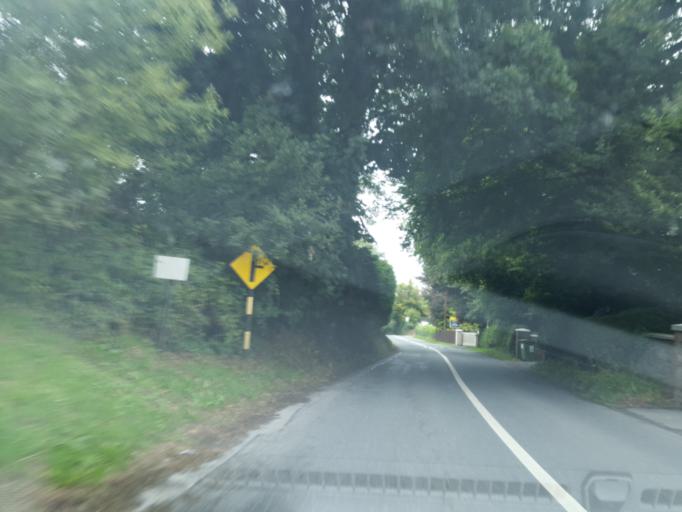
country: IE
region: Leinster
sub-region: Wicklow
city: Valleymount
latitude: 53.1265
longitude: -6.5805
